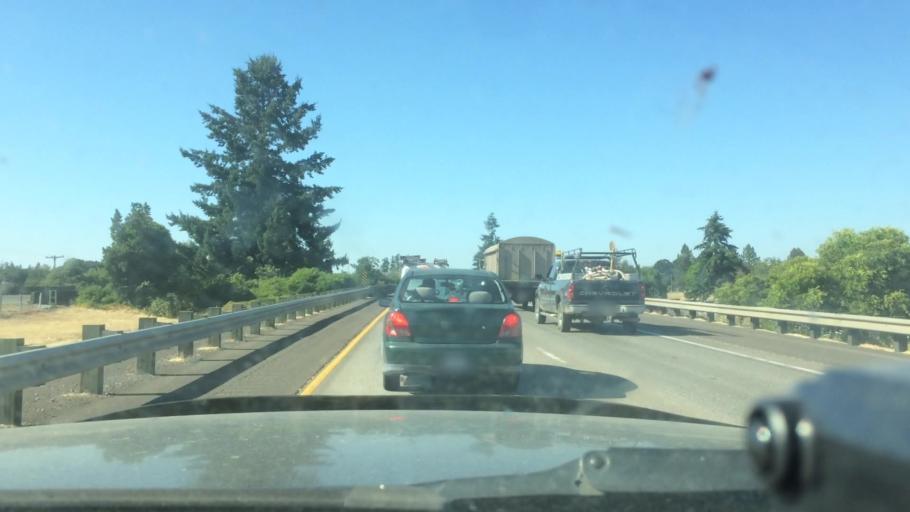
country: US
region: Oregon
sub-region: Linn County
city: Millersburg
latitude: 44.6430
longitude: -123.0625
